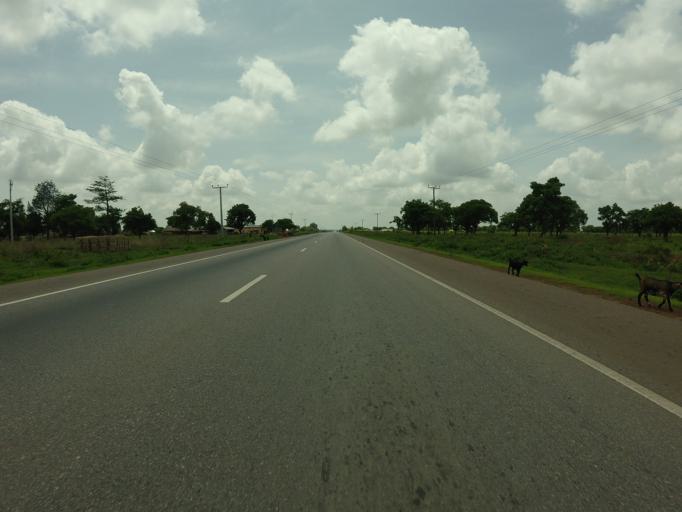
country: GH
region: Northern
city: Tamale
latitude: 9.2335
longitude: -1.0427
